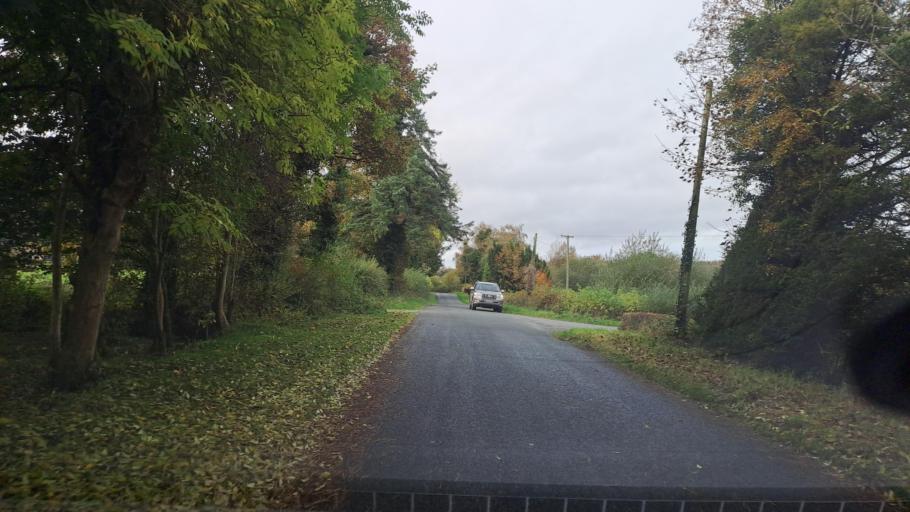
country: IE
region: Ulster
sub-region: An Cabhan
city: Bailieborough
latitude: 54.0485
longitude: -6.9086
